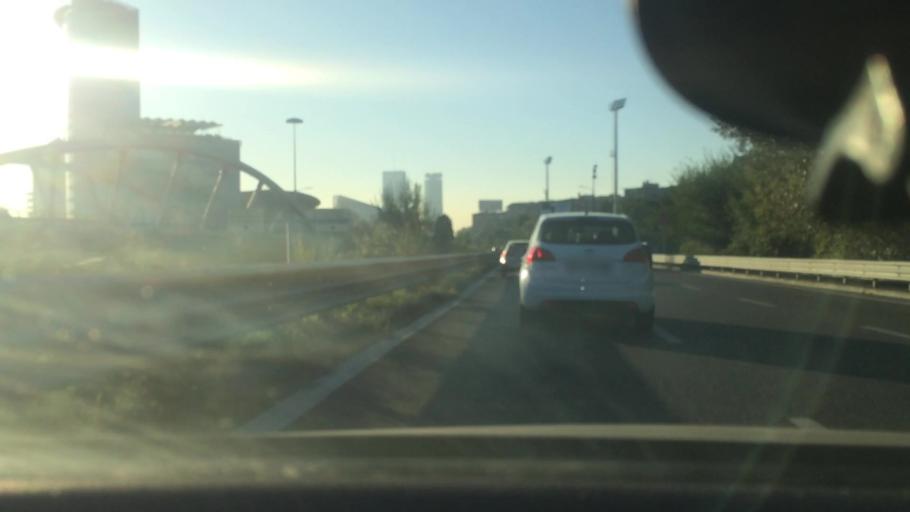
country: IT
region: Lombardy
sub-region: Citta metropolitana di Milano
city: Novate Milanese
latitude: 45.4914
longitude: 9.1367
